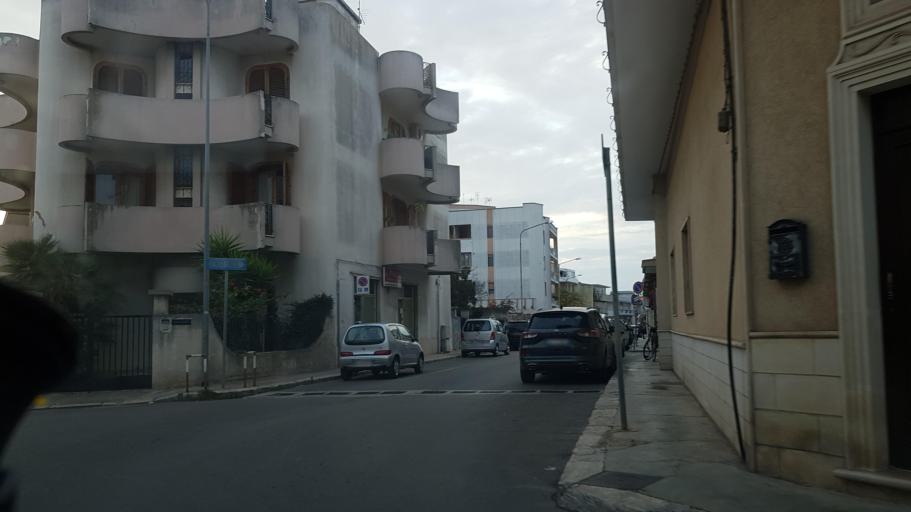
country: IT
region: Apulia
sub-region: Provincia di Brindisi
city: Mesagne
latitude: 40.5571
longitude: 17.8024
